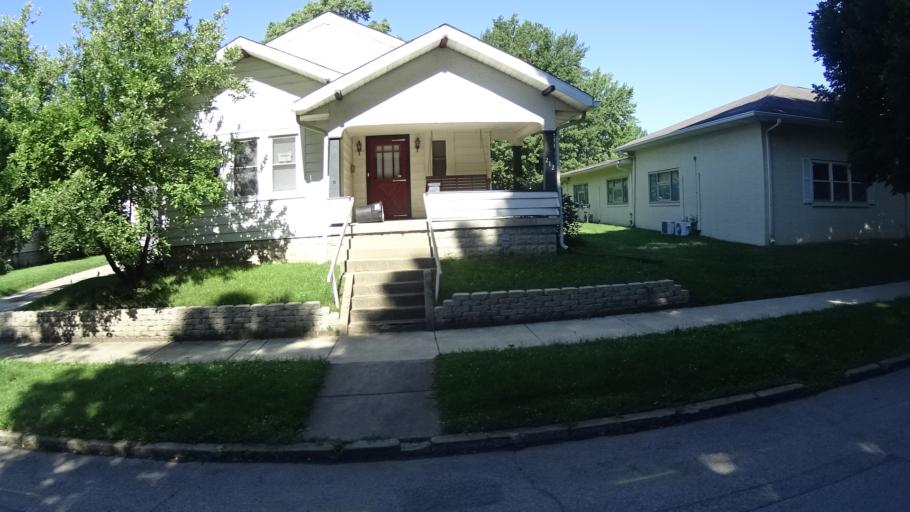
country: US
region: Indiana
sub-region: Madison County
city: Pendleton
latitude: 40.0007
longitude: -85.7473
